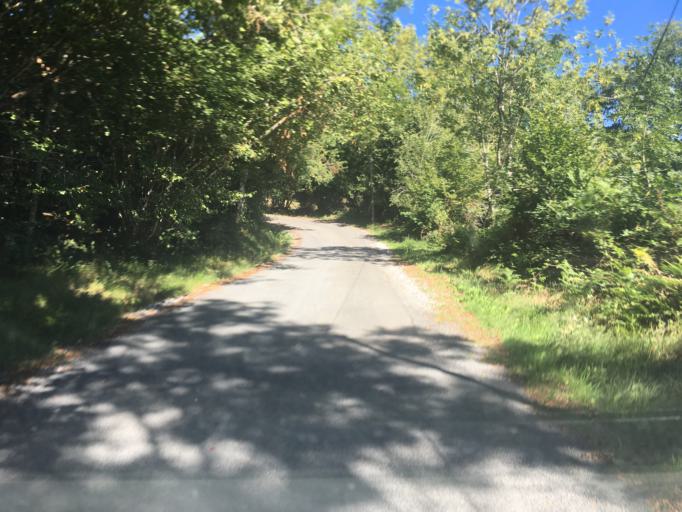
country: FR
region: Limousin
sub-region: Departement de la Correze
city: Bort-les-Orgues
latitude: 45.4029
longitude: 2.4835
